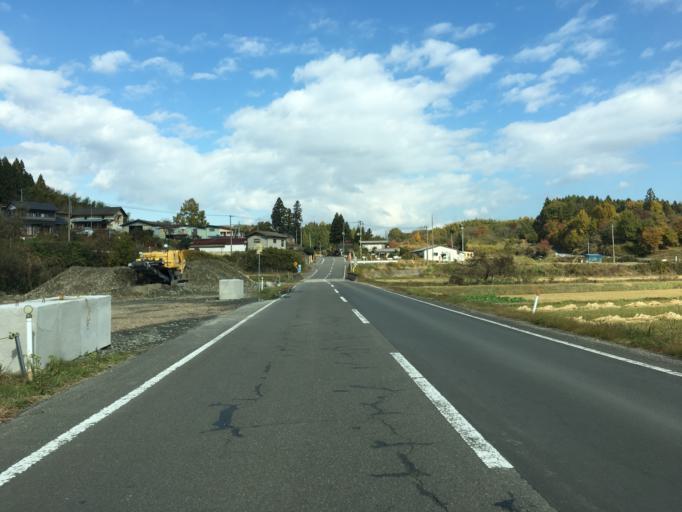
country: JP
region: Fukushima
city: Nihommatsu
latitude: 37.6359
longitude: 140.4728
